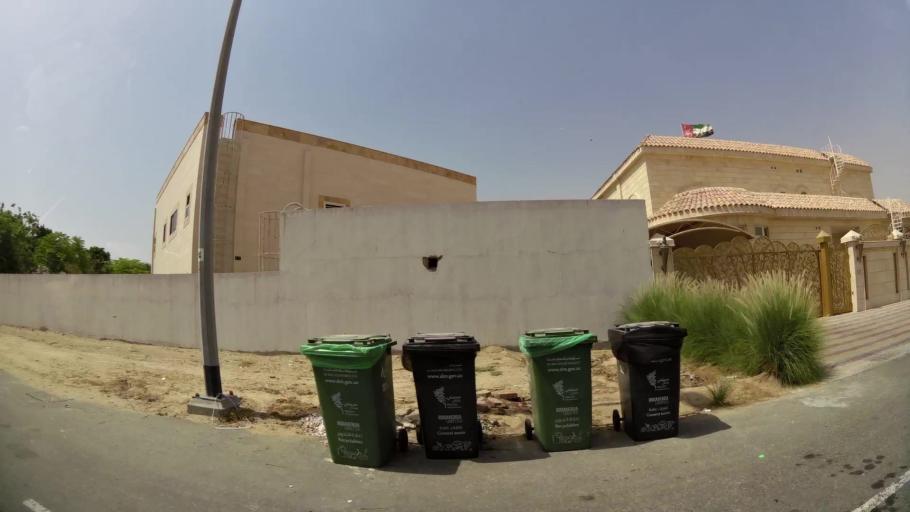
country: AE
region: Ash Shariqah
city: Sharjah
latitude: 25.2475
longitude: 55.4275
